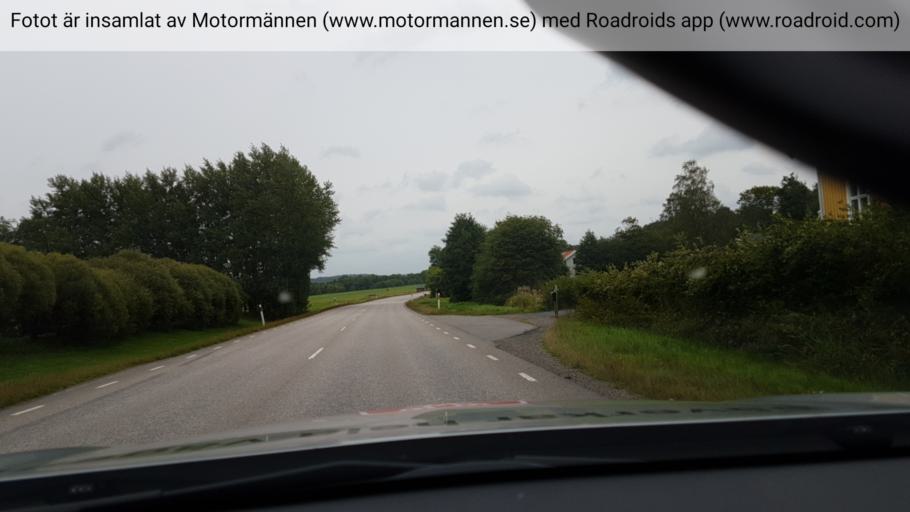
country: SE
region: Vaestra Goetaland
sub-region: Molndal
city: Lindome
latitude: 57.5862
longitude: 12.1184
